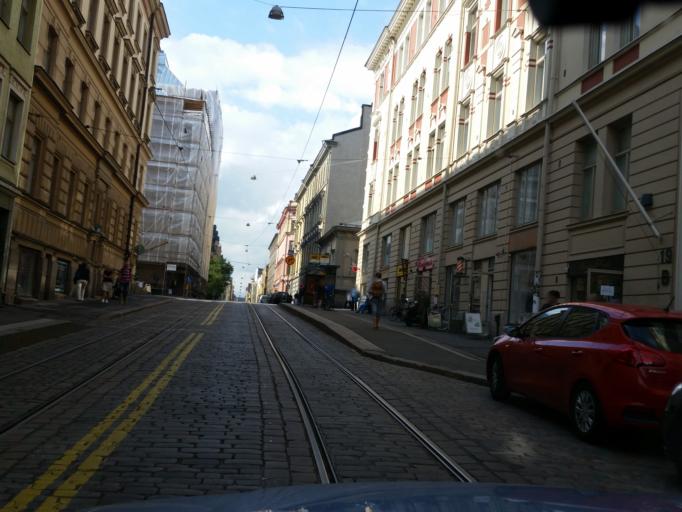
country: FI
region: Uusimaa
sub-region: Helsinki
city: Helsinki
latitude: 60.1609
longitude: 24.9417
